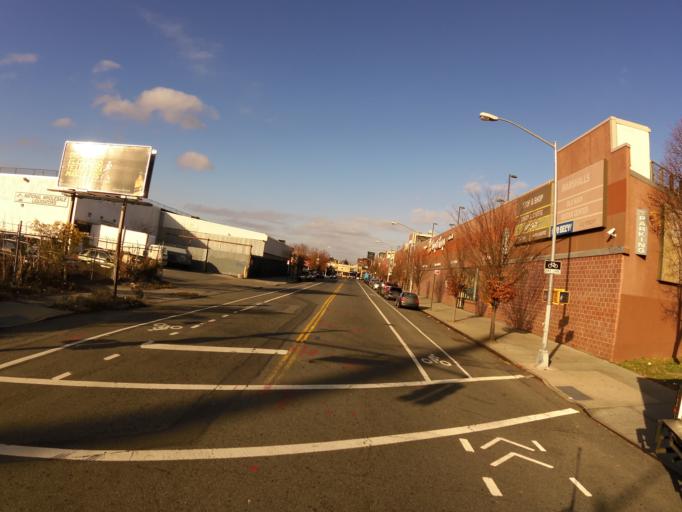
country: US
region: New York
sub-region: Queens County
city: Long Island City
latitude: 40.7512
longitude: -73.9152
